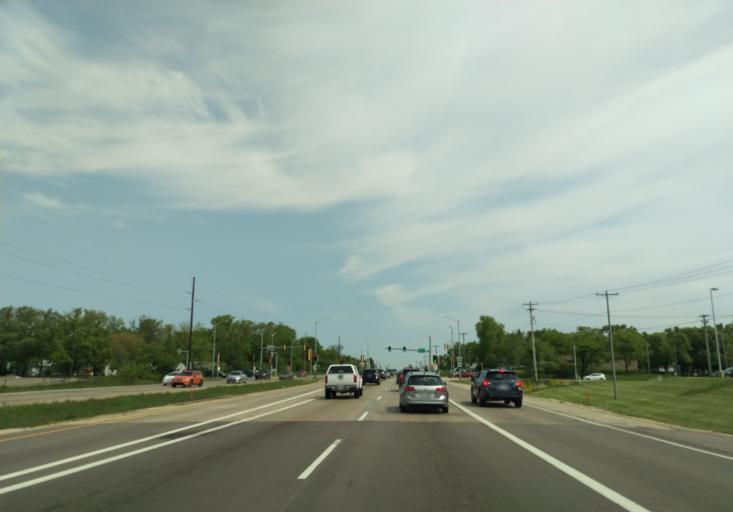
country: US
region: Wisconsin
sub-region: Dane County
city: Monona
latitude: 43.0722
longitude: -89.3095
